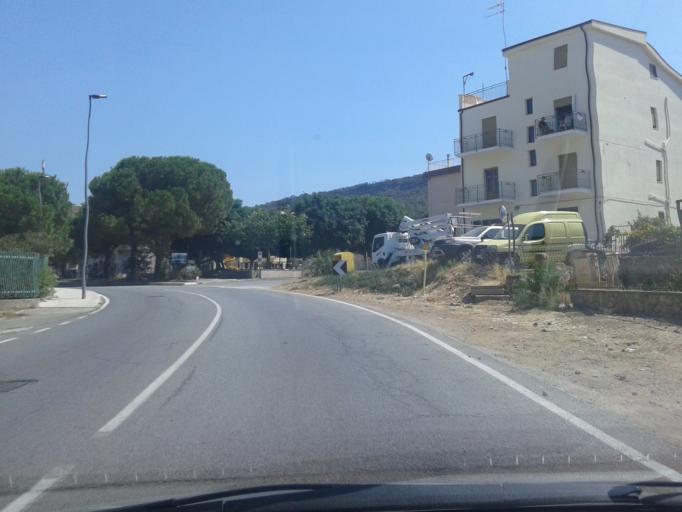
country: IT
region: Sicily
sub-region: Palermo
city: Finale
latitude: 38.0206
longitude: 14.1581
